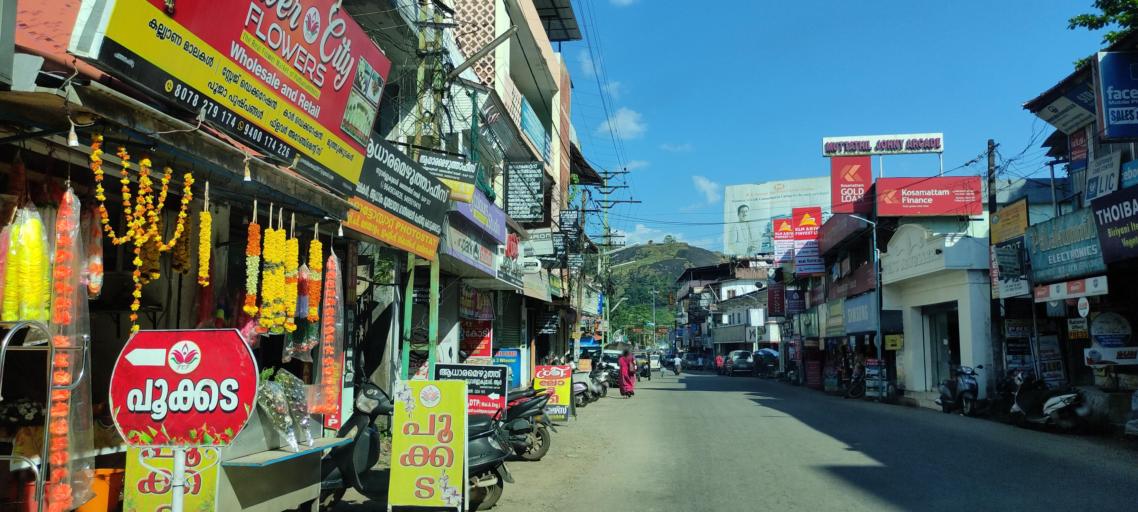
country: IN
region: Kerala
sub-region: Pattanamtitta
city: Pathanamthitta
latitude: 9.2649
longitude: 76.7883
